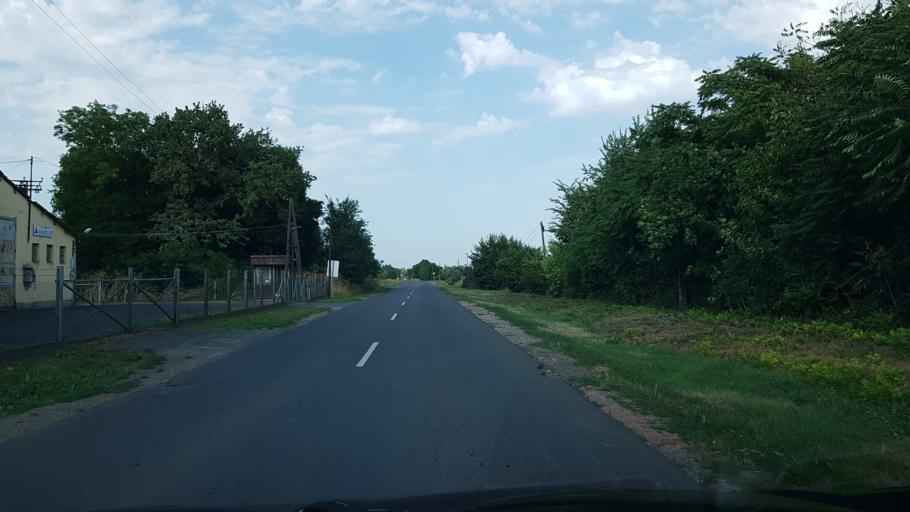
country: HU
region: Bekes
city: Fuzesgyarmat
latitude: 47.0853
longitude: 21.1988
